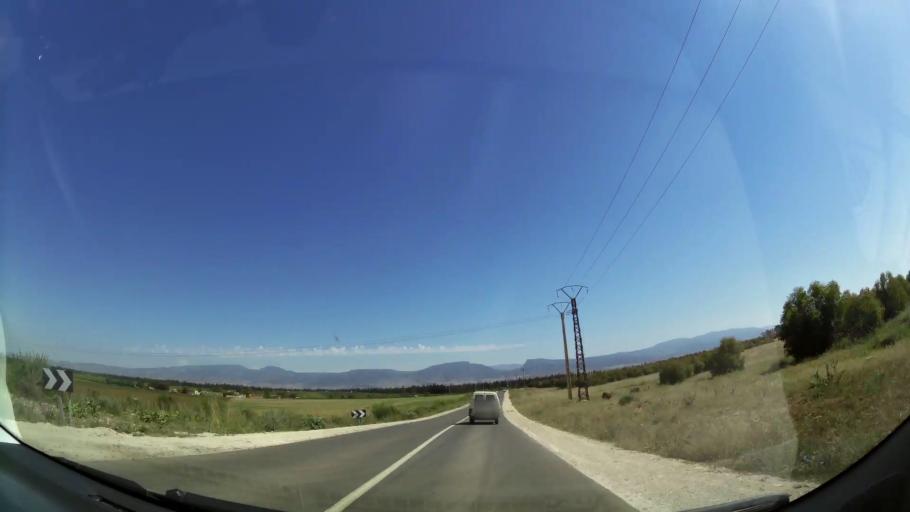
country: MA
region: Oriental
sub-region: Berkane-Taourirt
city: Madagh
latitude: 34.9962
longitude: -2.3942
